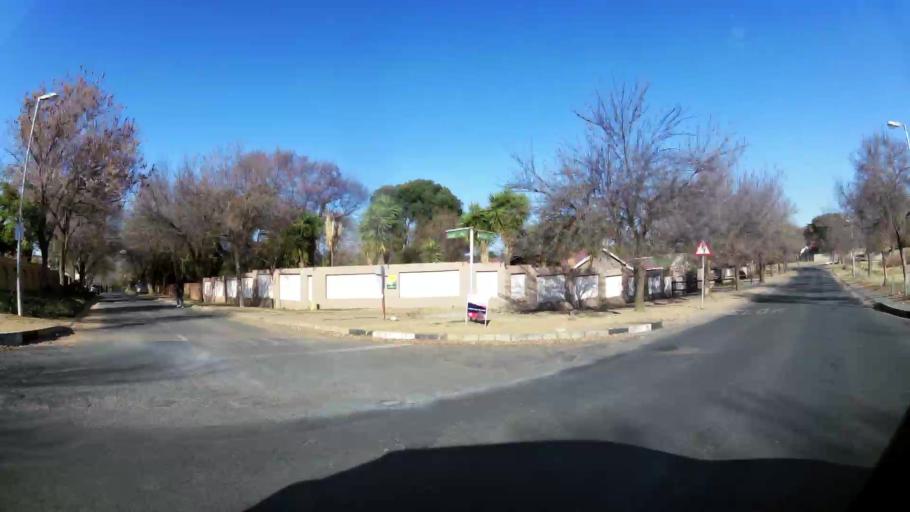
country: ZA
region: Gauteng
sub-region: City of Johannesburg Metropolitan Municipality
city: Roodepoort
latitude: -26.0886
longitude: 27.9620
